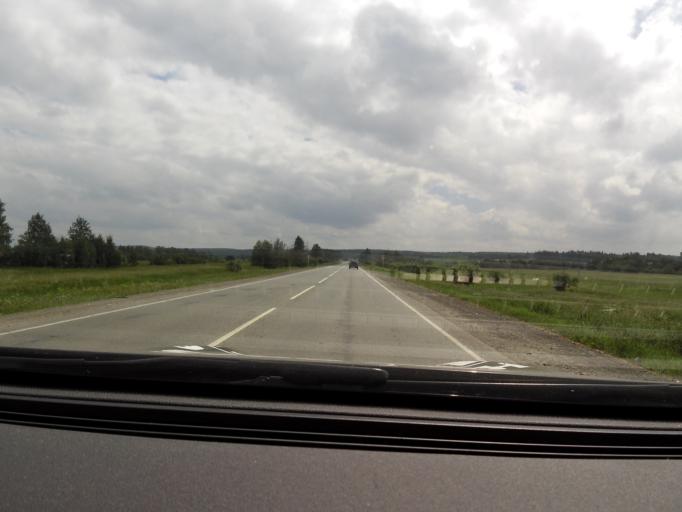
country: RU
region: Perm
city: Kukushtan
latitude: 57.5000
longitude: 56.6554
